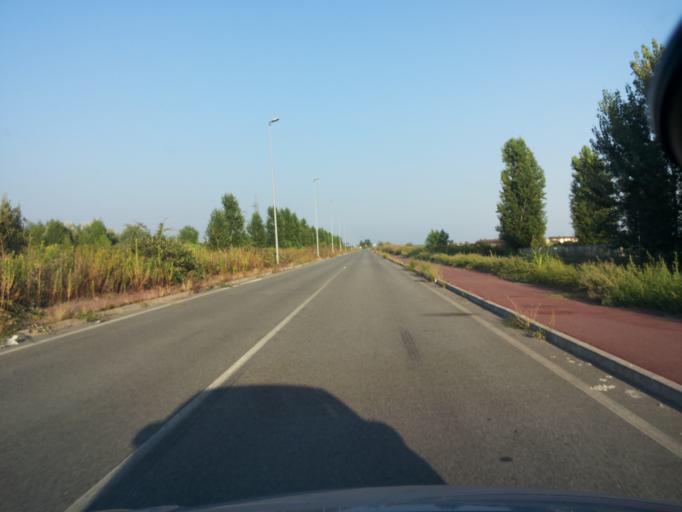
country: IT
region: Piedmont
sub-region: Provincia di Vercelli
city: Vercelli
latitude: 45.2965
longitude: 8.3964
